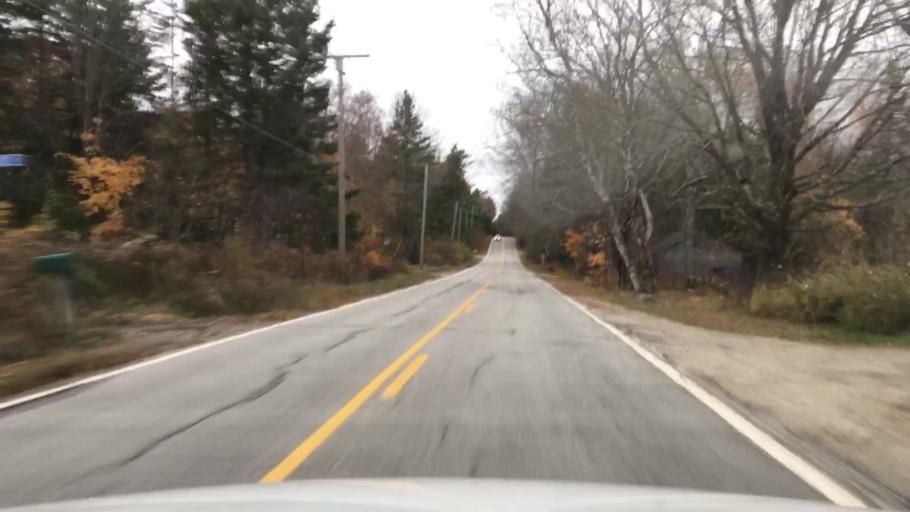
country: US
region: Maine
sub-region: Hancock County
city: Sedgwick
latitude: 44.3168
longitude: -68.5706
